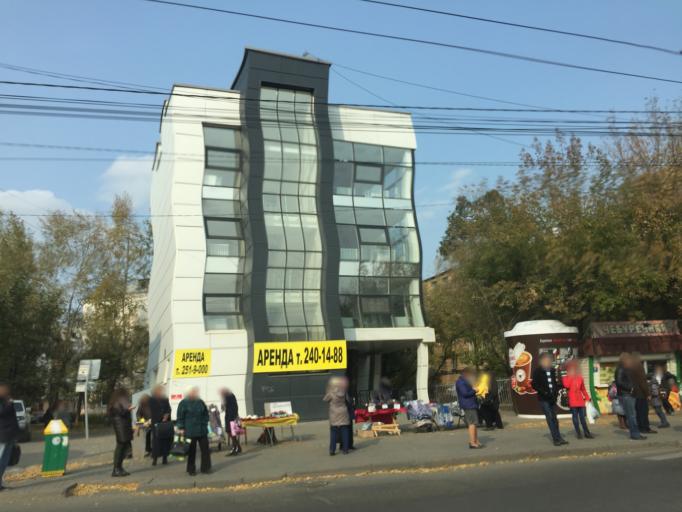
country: RU
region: Krasnoyarskiy
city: Krasnoyarsk
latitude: 56.0277
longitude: 92.9106
